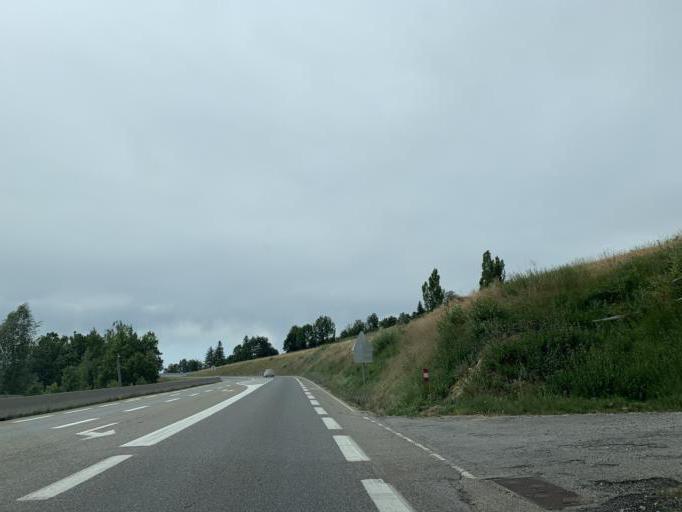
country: FR
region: Provence-Alpes-Cote d'Azur
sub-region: Departement des Hautes-Alpes
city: Gap
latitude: 44.5503
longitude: 6.0380
